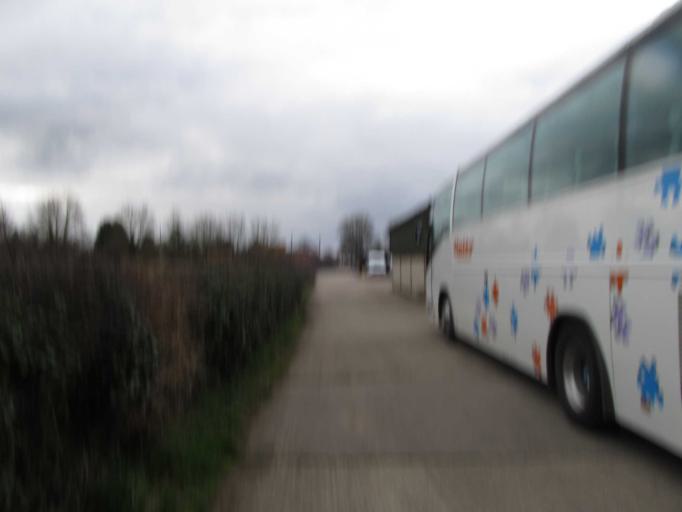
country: GB
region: England
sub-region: Nottinghamshire
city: Retford
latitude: 53.3848
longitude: -0.9003
